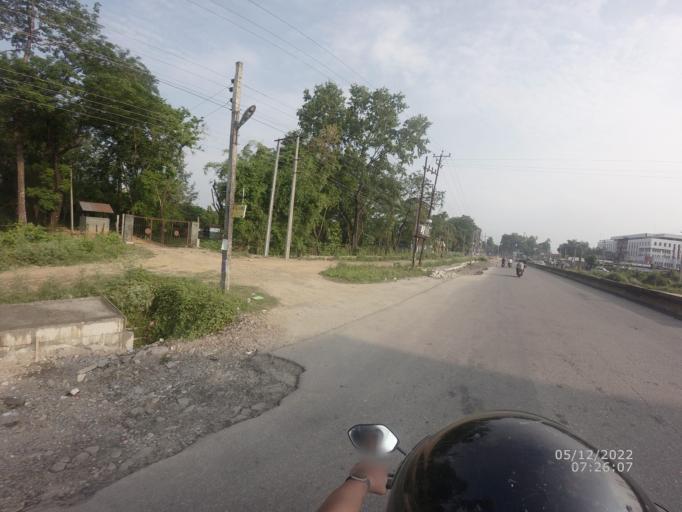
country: NP
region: Central Region
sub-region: Narayani Zone
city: Bharatpur
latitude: 27.6832
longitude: 84.4298
